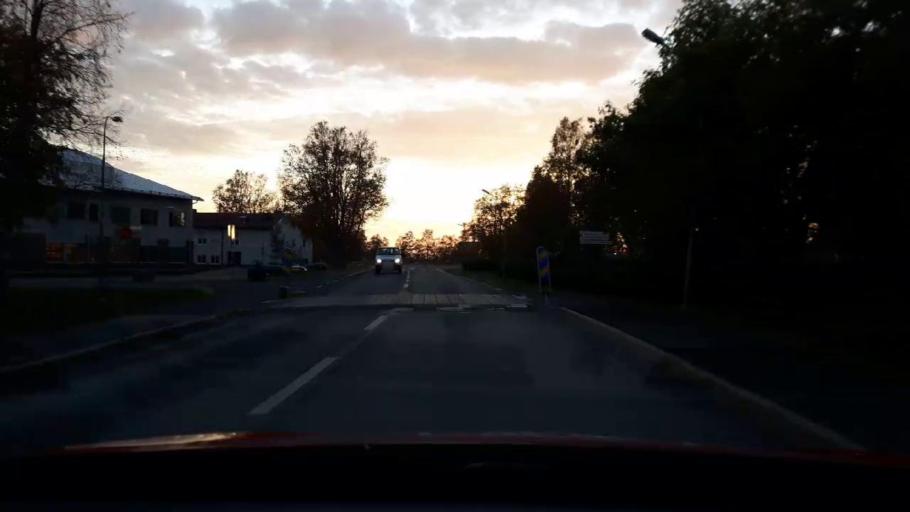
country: SE
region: Jaemtland
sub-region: OEstersunds Kommun
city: Ostersund
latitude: 63.2480
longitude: 14.5659
